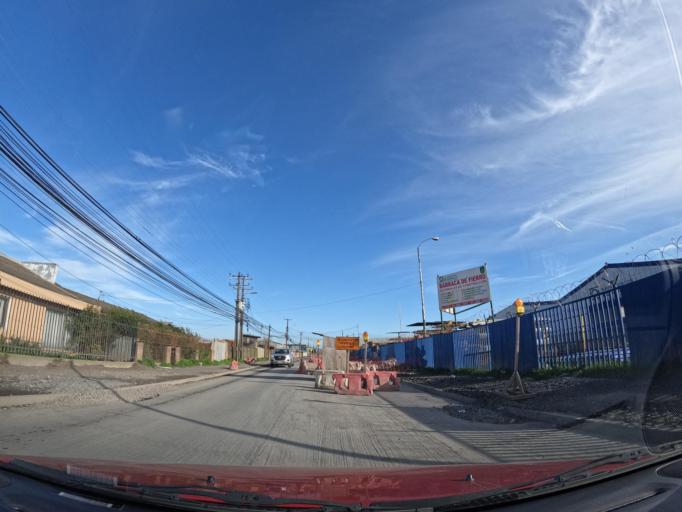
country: CL
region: Biobio
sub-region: Provincia de Concepcion
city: Talcahuano
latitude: -36.7635
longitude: -73.0814
